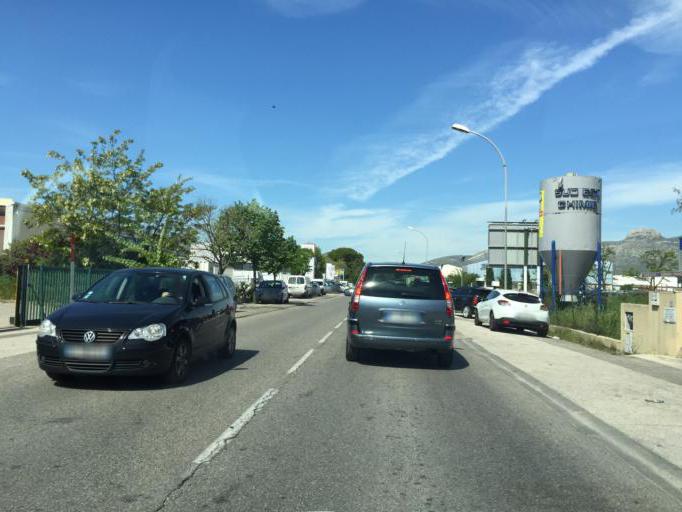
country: FR
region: Provence-Alpes-Cote d'Azur
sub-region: Departement des Bouches-du-Rhone
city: Aubagne
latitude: 43.2895
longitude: 5.5982
